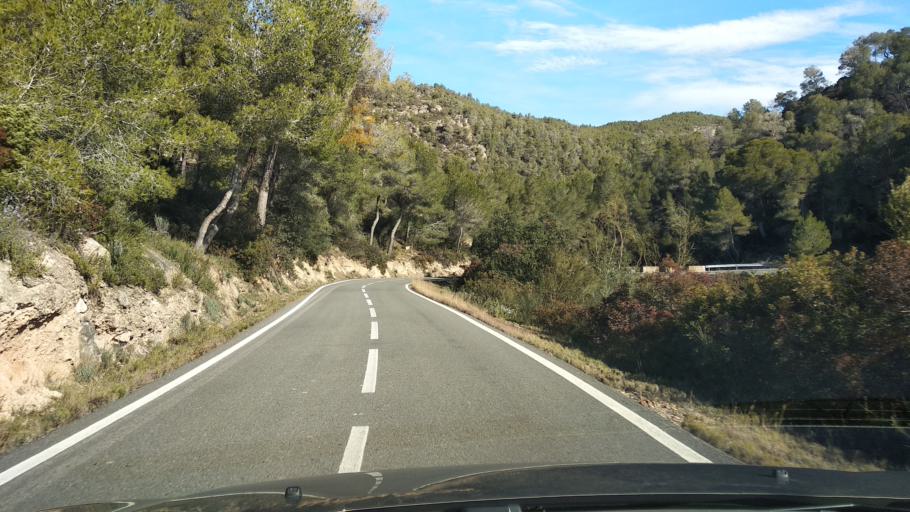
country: ES
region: Catalonia
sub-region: Provincia de Tarragona
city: el Masroig
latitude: 41.1720
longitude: 0.7139
